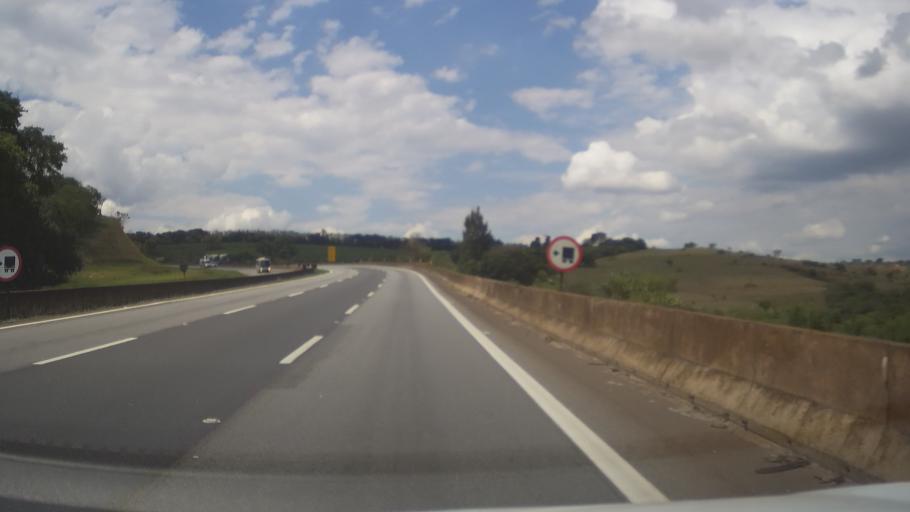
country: BR
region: Minas Gerais
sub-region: Nepomuceno
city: Nepomuceno
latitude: -21.2865
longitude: -45.1414
